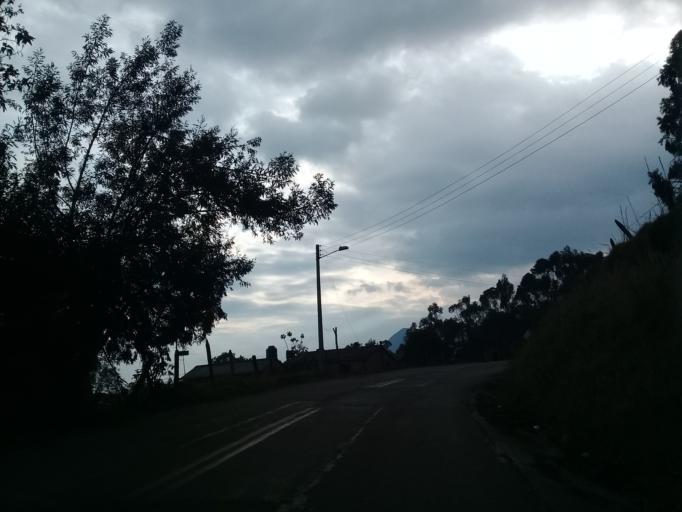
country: CO
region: Cundinamarca
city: Zipaquira
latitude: 5.0410
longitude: -74.0473
